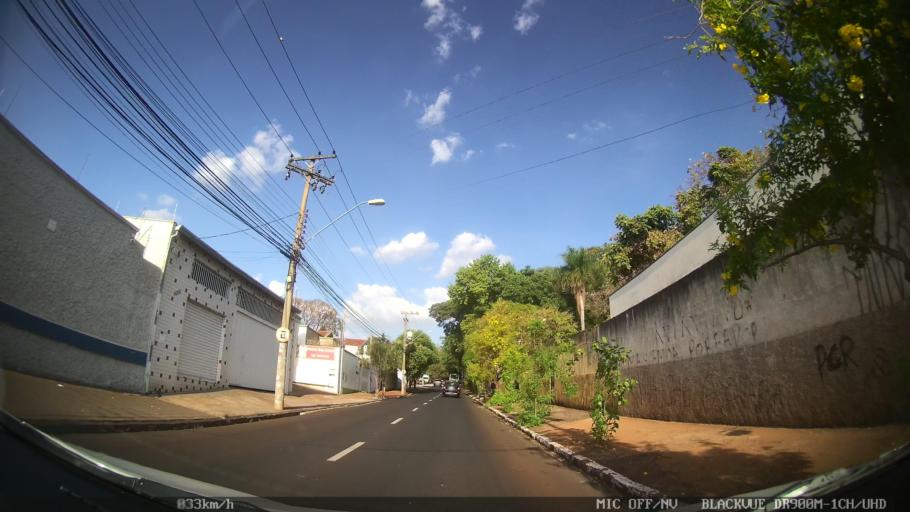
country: BR
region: Sao Paulo
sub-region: Ribeirao Preto
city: Ribeirao Preto
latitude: -21.1697
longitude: -47.8019
